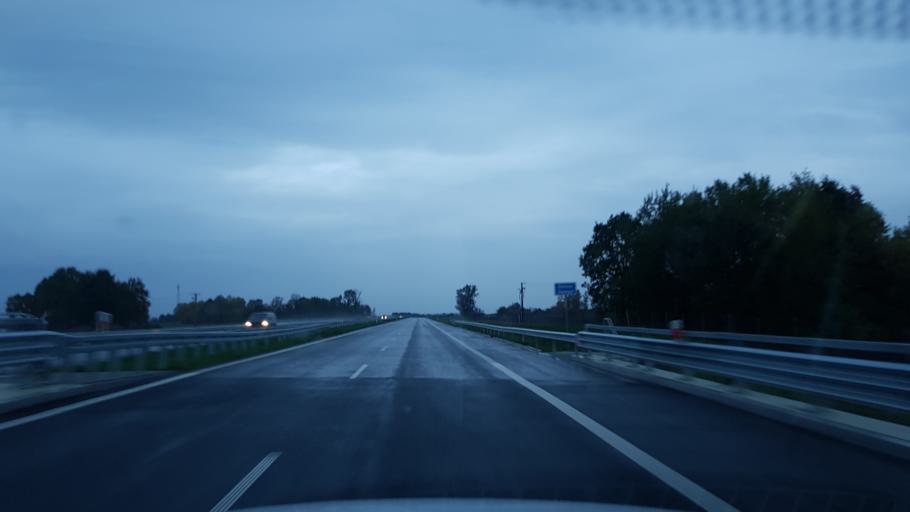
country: PL
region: West Pomeranian Voivodeship
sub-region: Powiat kolobrzeski
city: Ryman
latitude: 54.0161
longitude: 15.4766
